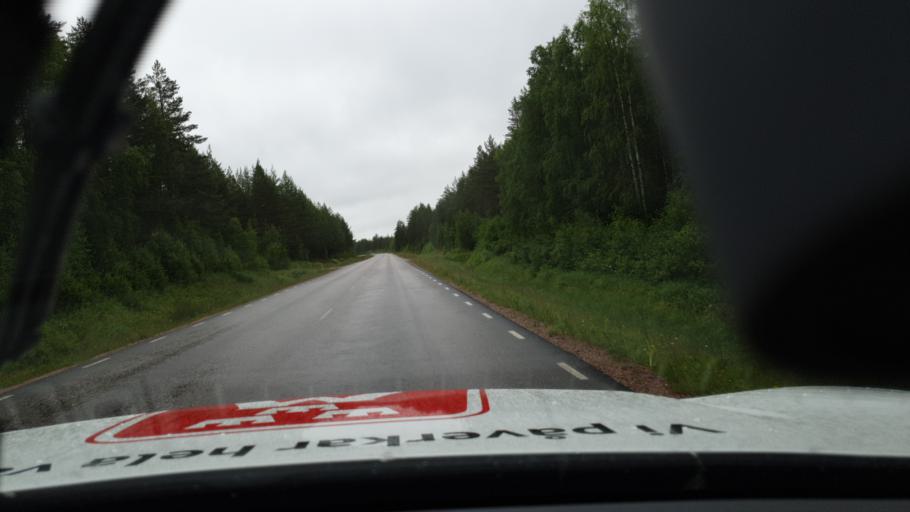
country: SE
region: Norrbotten
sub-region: Overtornea Kommun
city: OEvertornea
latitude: 66.4780
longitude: 23.6894
